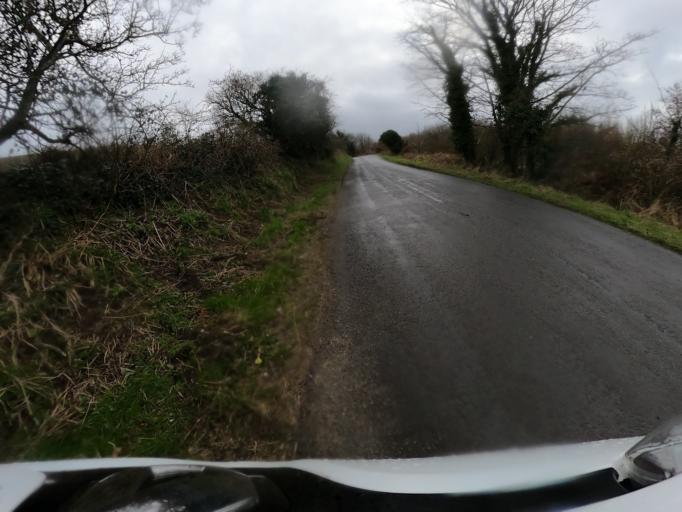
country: IM
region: Ramsey
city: Ramsey
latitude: 54.3824
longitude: -4.4500
